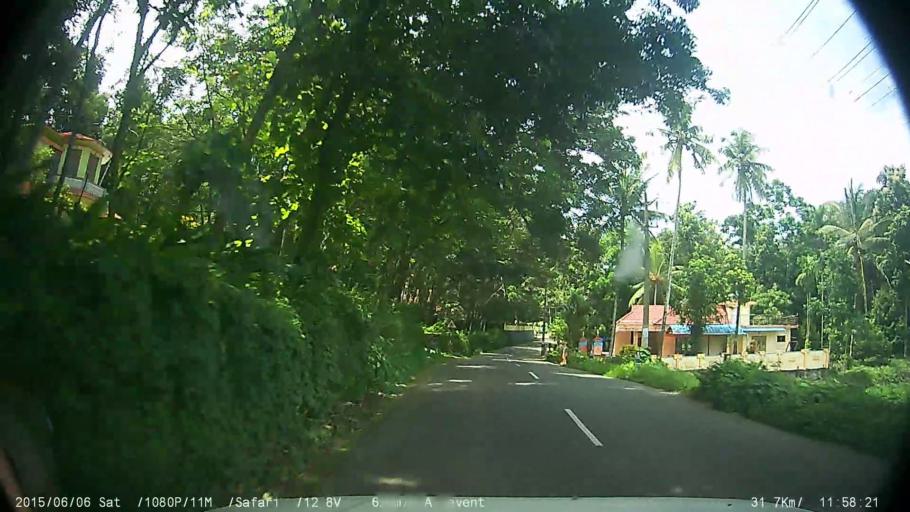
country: IN
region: Kerala
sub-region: Kottayam
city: Palackattumala
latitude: 9.7570
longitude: 76.5929
